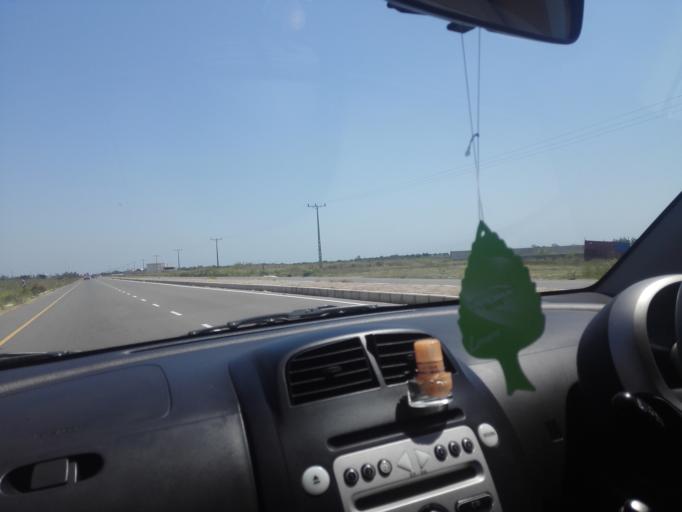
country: MZ
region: Maputo City
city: Maputo
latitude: -25.8315
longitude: 32.6720
